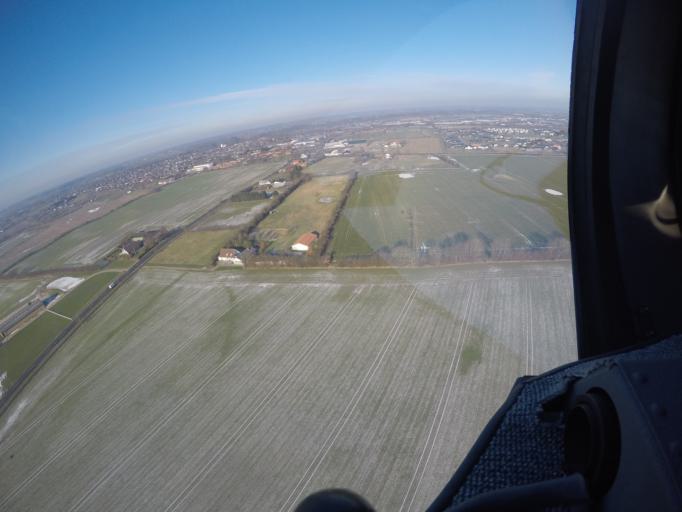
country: DK
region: South Denmark
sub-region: Fredericia Kommune
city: Taulov
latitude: 55.5269
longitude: 9.6258
